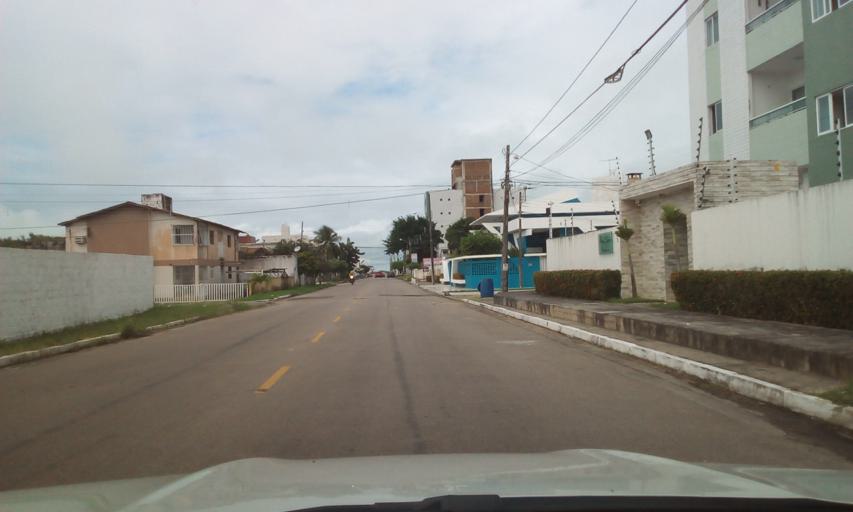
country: BR
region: Paraiba
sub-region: Joao Pessoa
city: Joao Pessoa
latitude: -7.0595
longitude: -34.8466
